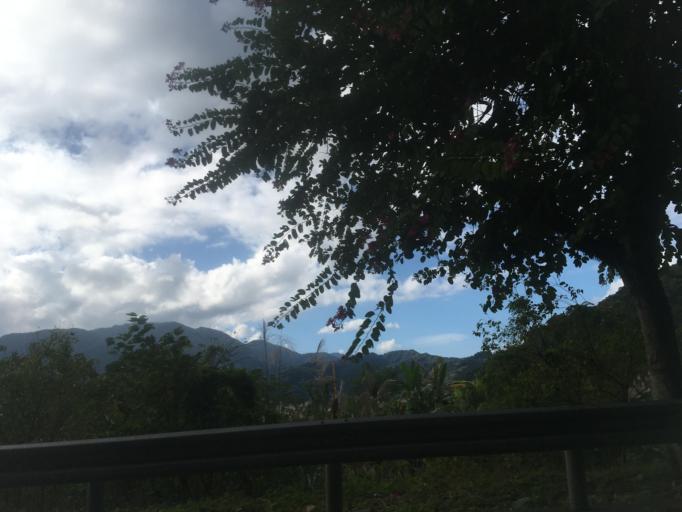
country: TW
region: Taiwan
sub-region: Yilan
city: Yilan
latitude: 24.6555
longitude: 121.5828
